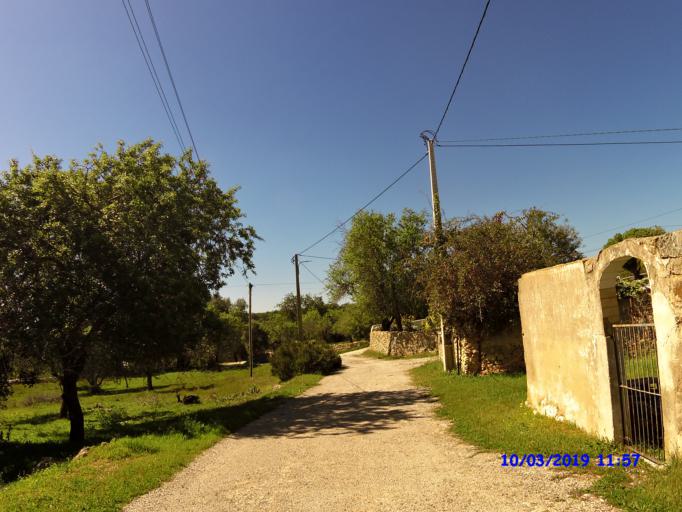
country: PT
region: Faro
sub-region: Loule
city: Boliqueime
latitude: 37.1637
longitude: -8.1419
